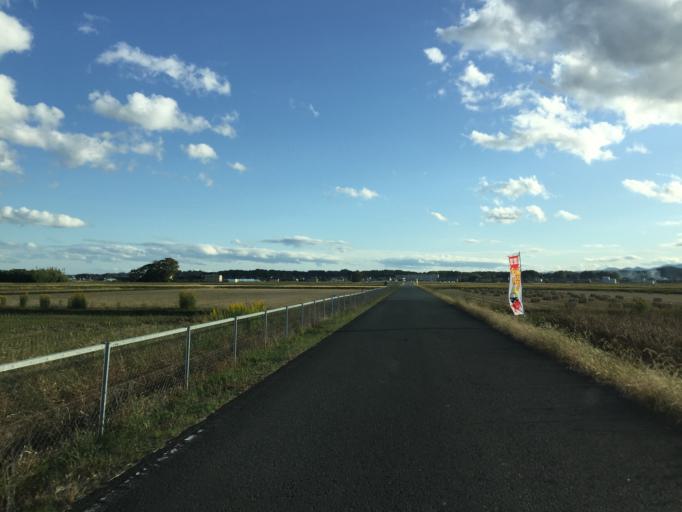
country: JP
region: Miyagi
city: Marumori
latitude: 37.7984
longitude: 140.9487
